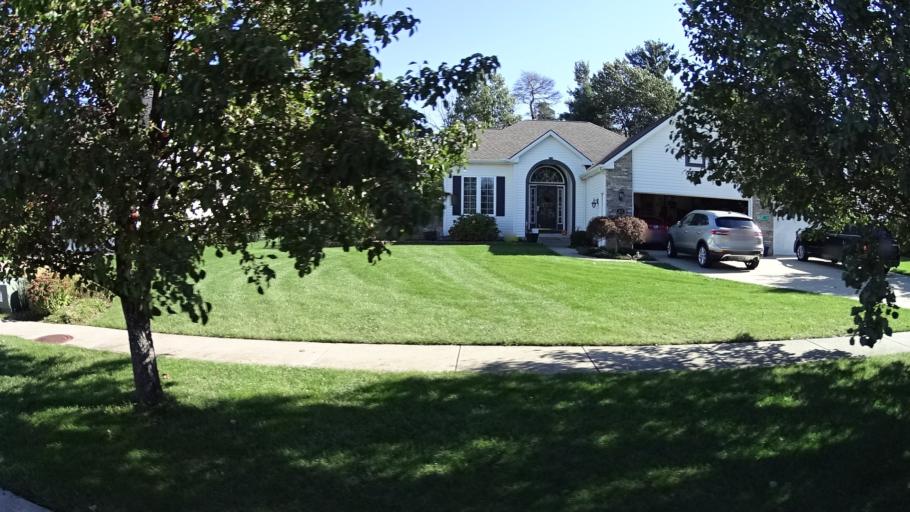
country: US
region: Ohio
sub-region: Lorain County
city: Amherst
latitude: 41.3832
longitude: -82.2423
